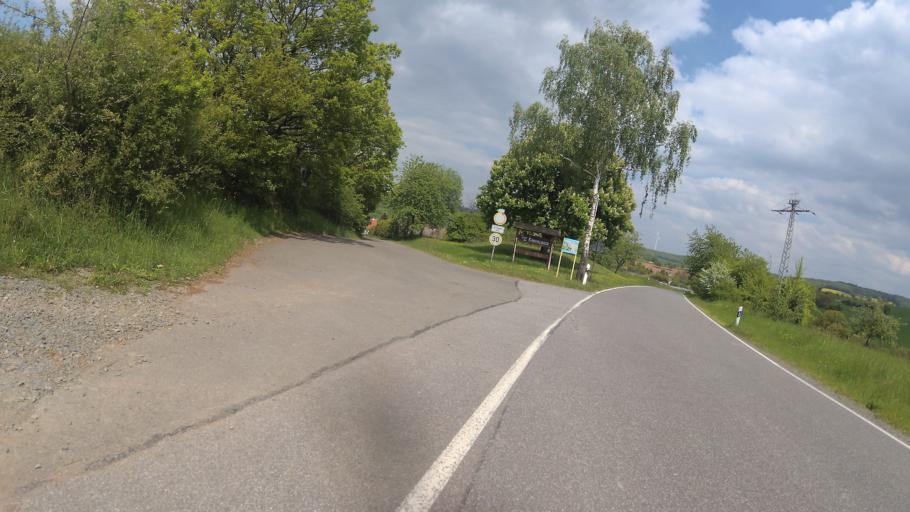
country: DE
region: Rheinland-Pfalz
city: Krottelbach
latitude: 49.4631
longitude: 7.3258
